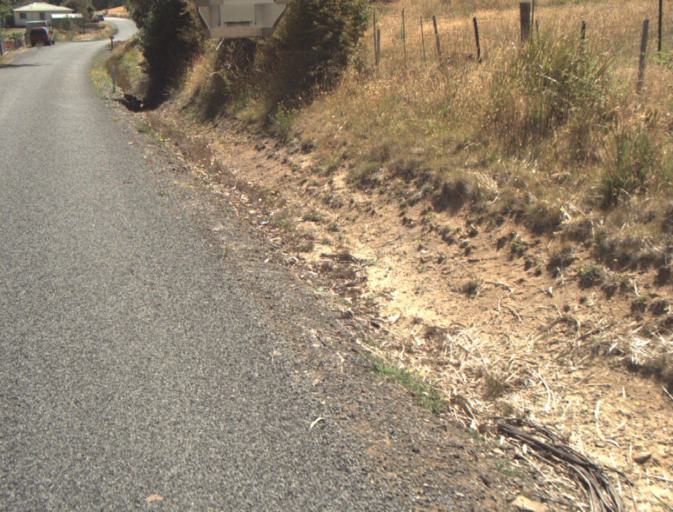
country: AU
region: Tasmania
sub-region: Launceston
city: Newstead
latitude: -41.3554
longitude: 147.3031
